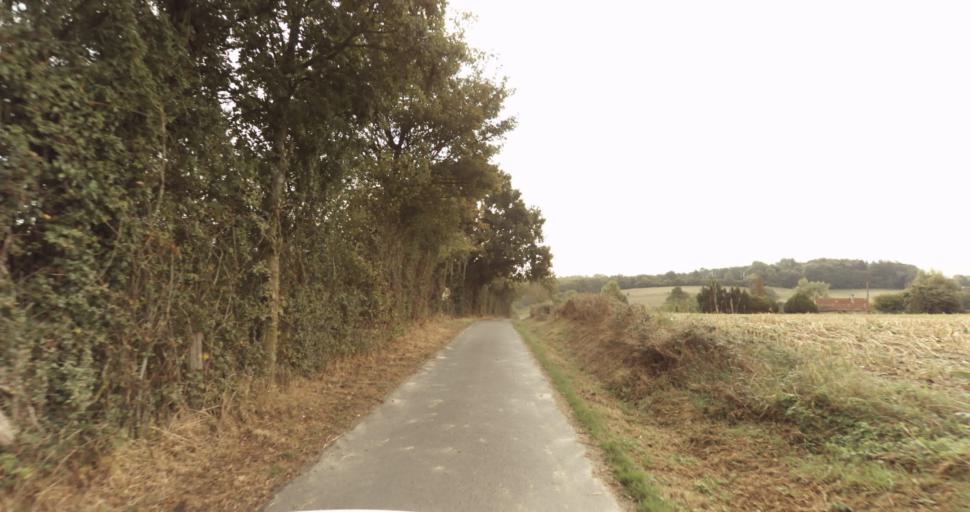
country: FR
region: Lower Normandy
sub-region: Departement de l'Orne
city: Trun
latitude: 48.8981
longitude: 0.0960
